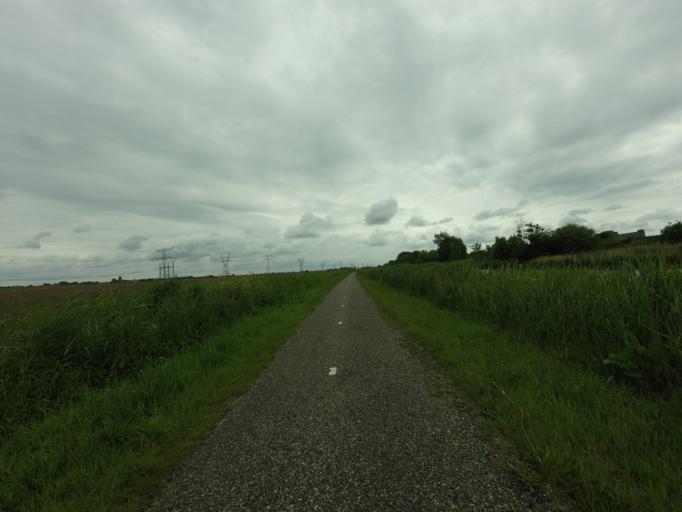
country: NL
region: North Holland
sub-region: Gemeente Waterland
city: Broek in Waterland
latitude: 52.3983
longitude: 4.9656
